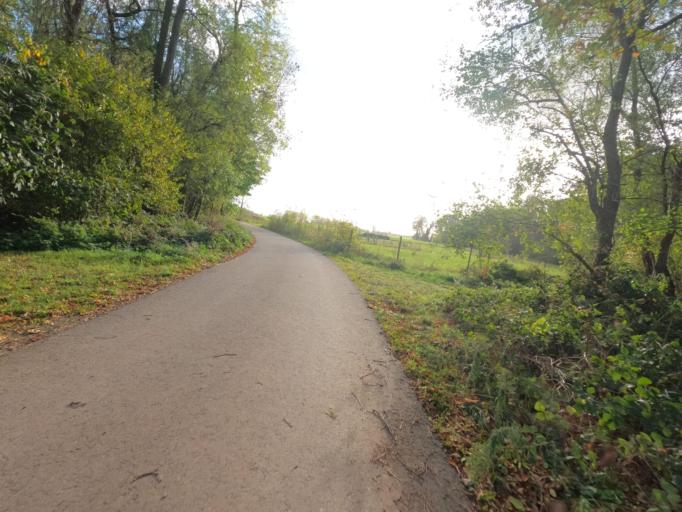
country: DE
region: North Rhine-Westphalia
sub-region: Regierungsbezirk Koln
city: Titz
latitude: 51.0858
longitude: 6.4063
